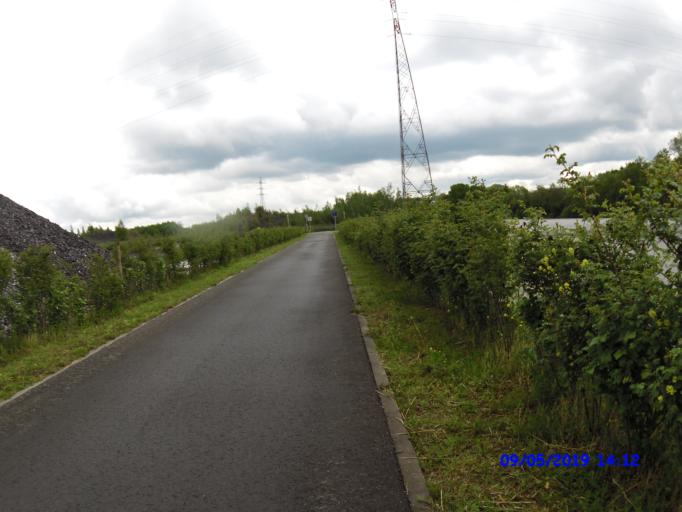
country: BE
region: Wallonia
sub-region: Province du Hainaut
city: Aiseau
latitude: 50.4407
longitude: 4.5753
